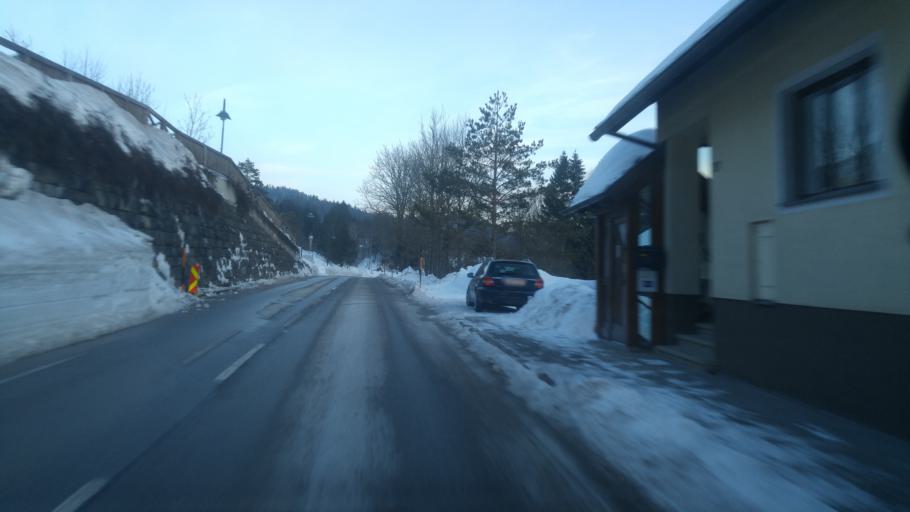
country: AT
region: Lower Austria
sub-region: Politischer Bezirk Wiener Neustadt
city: Rohr im Gebirge
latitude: 47.8946
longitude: 15.7388
